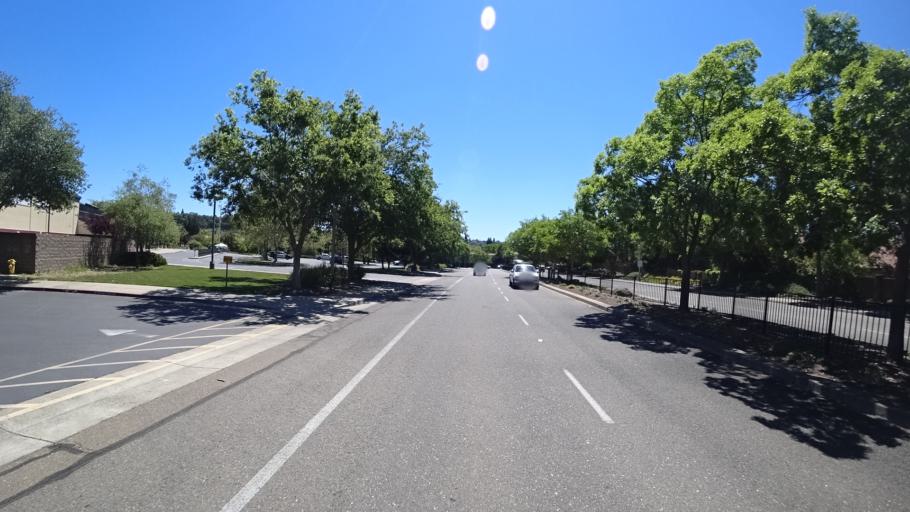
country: US
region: California
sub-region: Placer County
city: Rocklin
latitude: 38.8208
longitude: -121.2542
